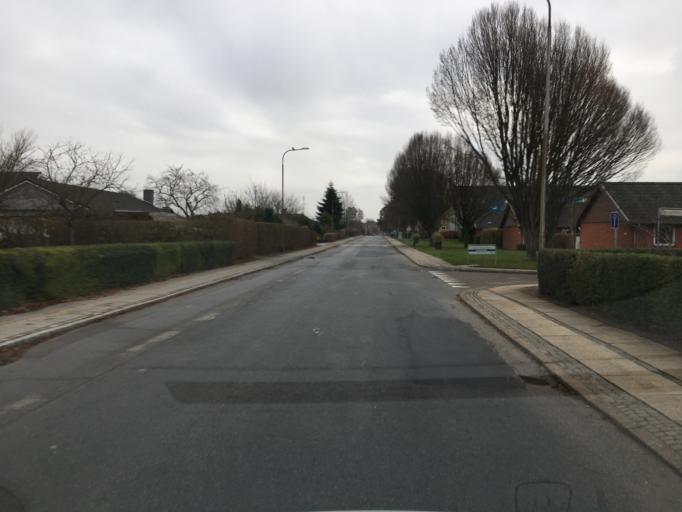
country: DK
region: South Denmark
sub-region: Tonder Kommune
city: Tonder
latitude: 54.9442
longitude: 8.8614
